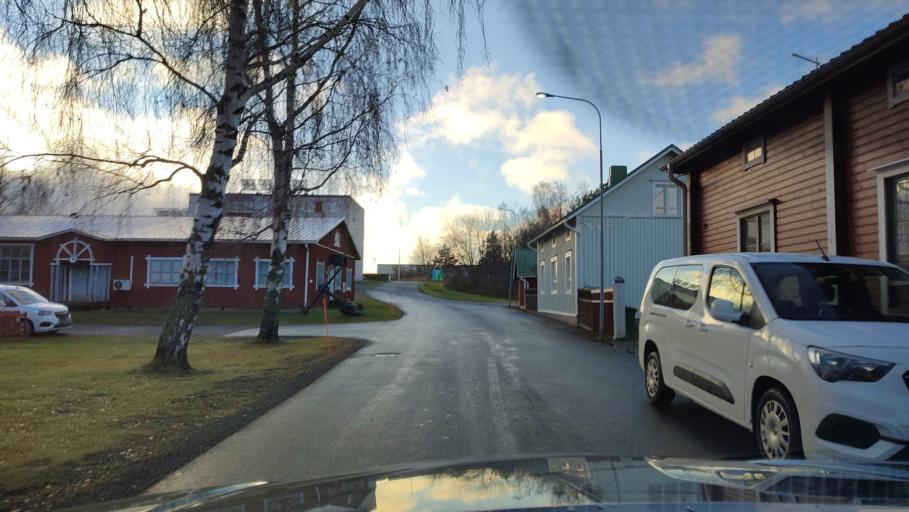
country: FI
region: Ostrobothnia
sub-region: Sydosterbotten
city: Kristinestad
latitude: 62.2686
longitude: 21.3772
